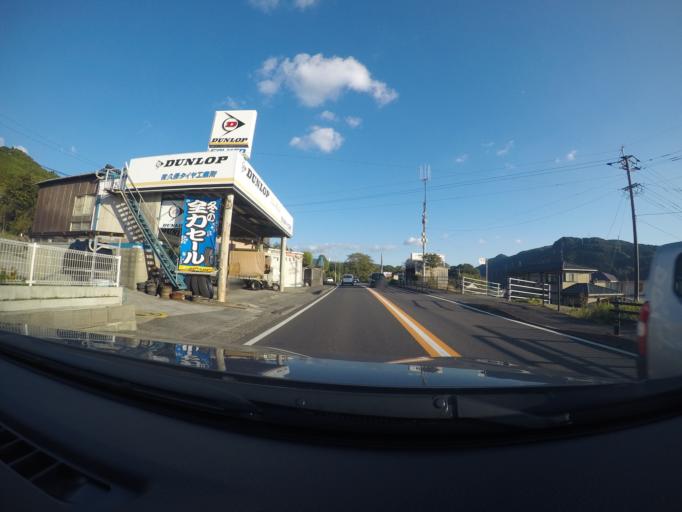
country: JP
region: Kumamoto
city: Minamata
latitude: 32.2105
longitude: 130.4118
